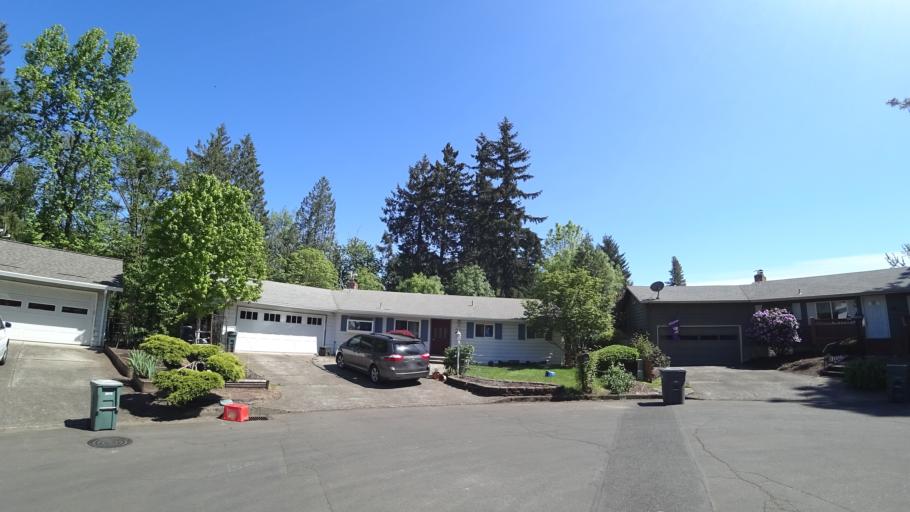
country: US
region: Oregon
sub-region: Washington County
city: Hillsboro
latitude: 45.5134
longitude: -122.9554
